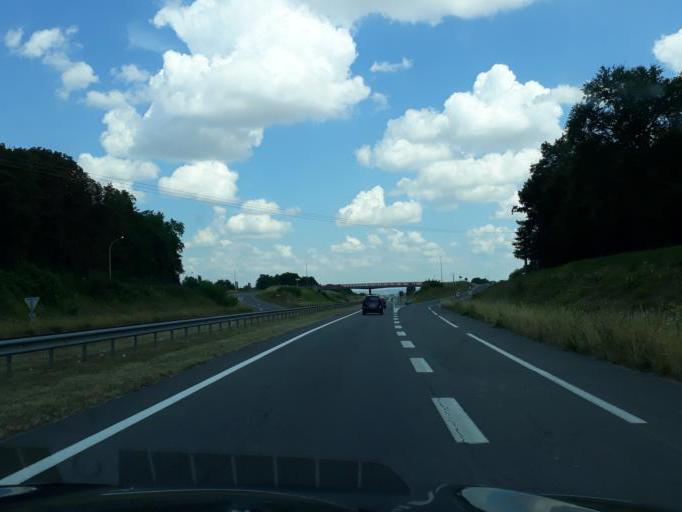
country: FR
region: Centre
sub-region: Departement du Cher
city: Bourges
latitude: 47.0646
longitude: 2.4320
